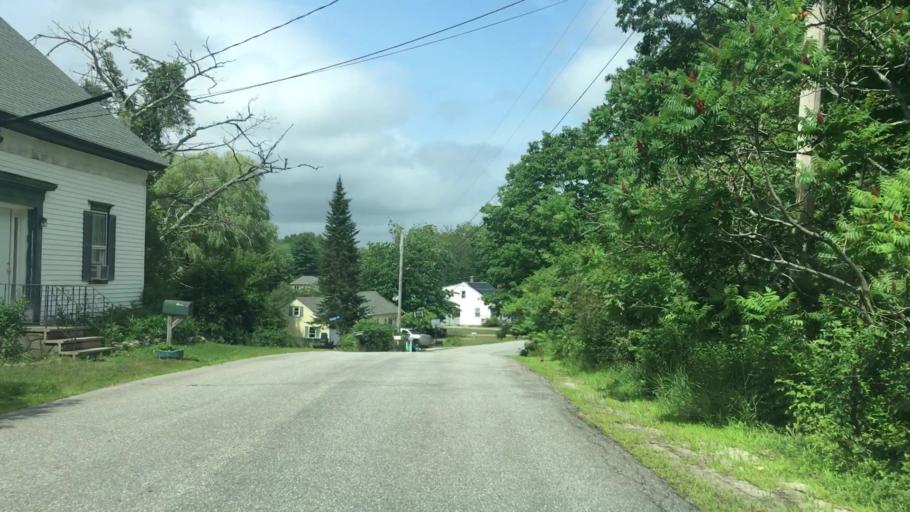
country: US
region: Maine
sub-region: Cumberland County
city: Brunswick
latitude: 43.8903
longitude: -69.9078
